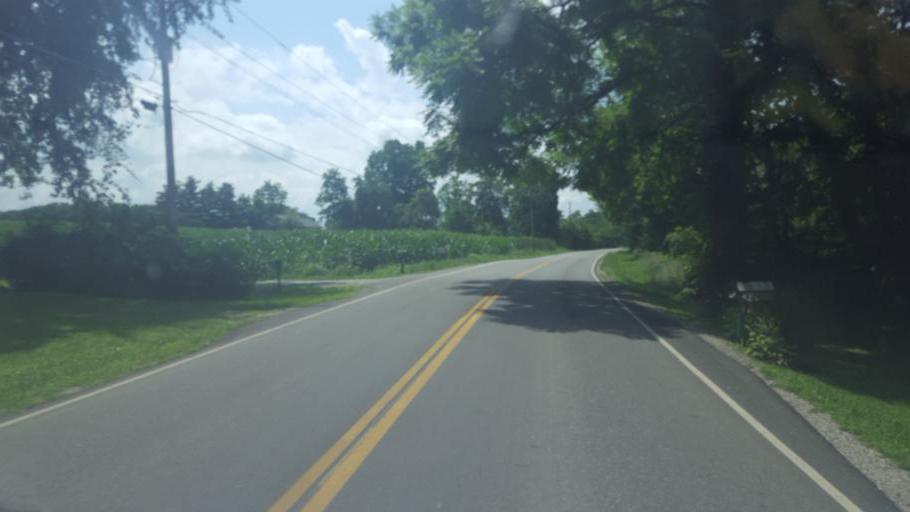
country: US
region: Ohio
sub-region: Ross County
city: Kingston
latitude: 39.5301
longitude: -82.7709
